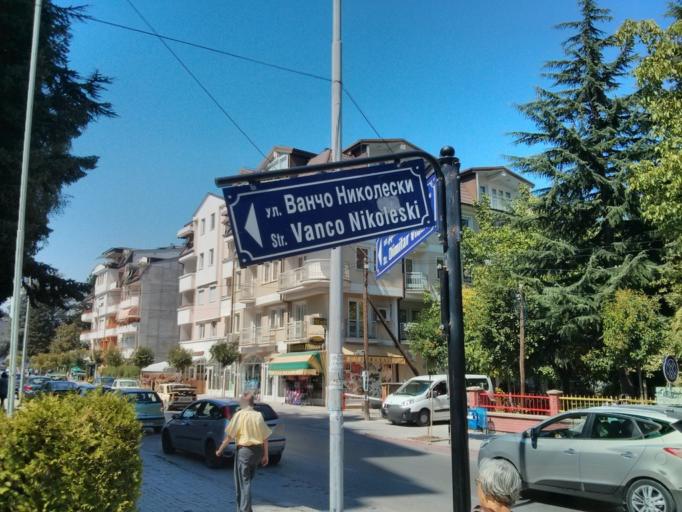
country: MK
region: Ohrid
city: Ohrid
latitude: 41.1130
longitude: 20.8051
